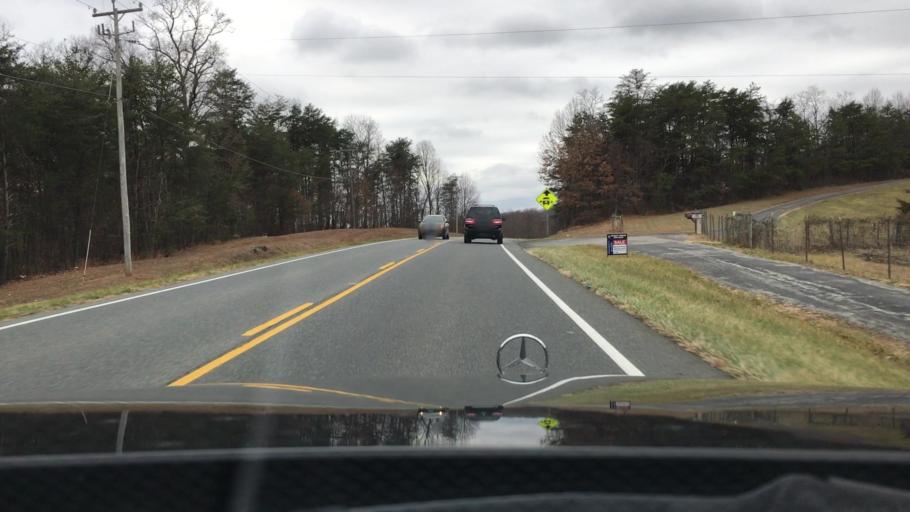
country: US
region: Virginia
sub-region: Franklin County
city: North Shore
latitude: 37.2437
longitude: -79.6789
